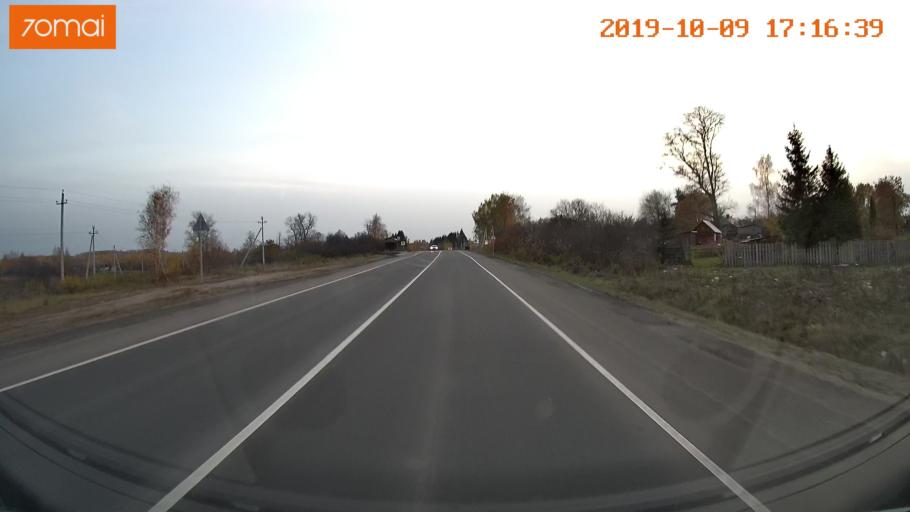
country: RU
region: Ivanovo
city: Furmanov
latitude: 57.2858
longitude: 41.1625
